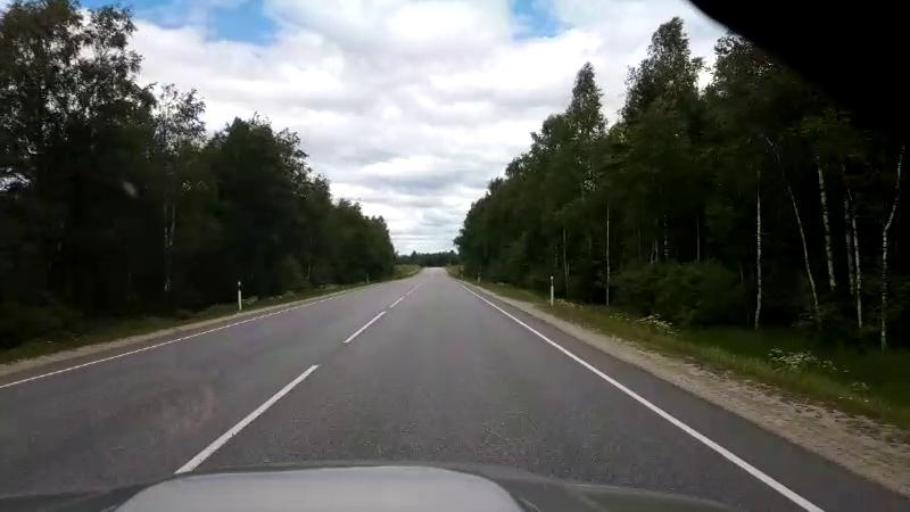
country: EE
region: Raplamaa
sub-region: Maerjamaa vald
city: Marjamaa
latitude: 58.9585
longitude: 24.4738
